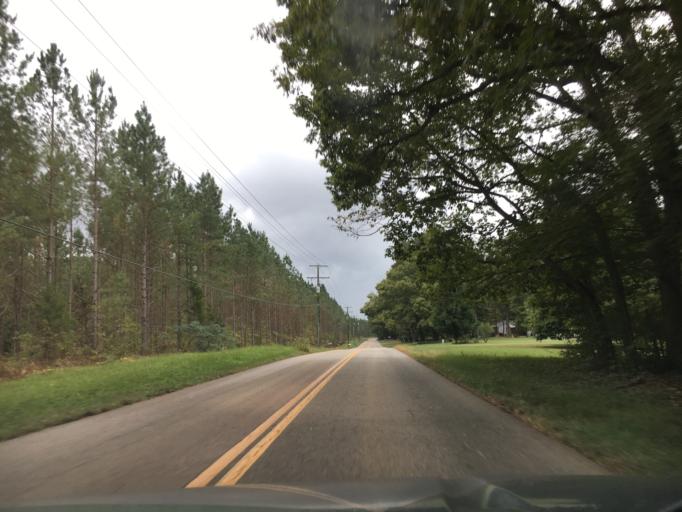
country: US
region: Virginia
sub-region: Amelia County
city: Amelia Court House
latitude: 37.3653
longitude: -77.9765
